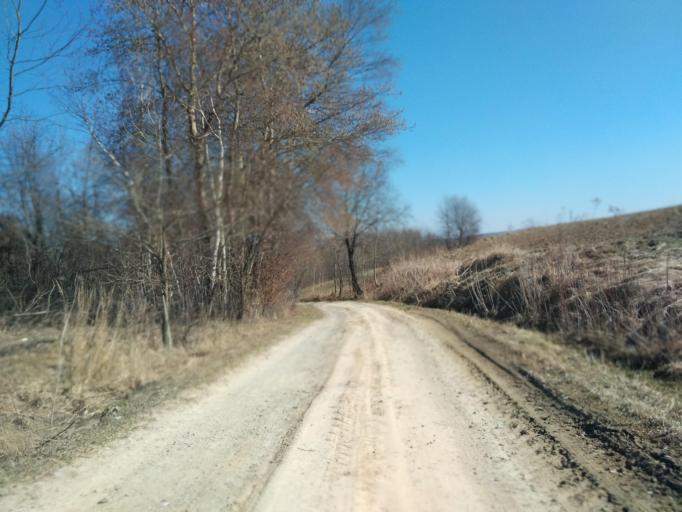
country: PL
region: Subcarpathian Voivodeship
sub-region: Powiat ropczycko-sedziszowski
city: Wielopole Skrzynskie
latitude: 49.9501
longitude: 21.5758
